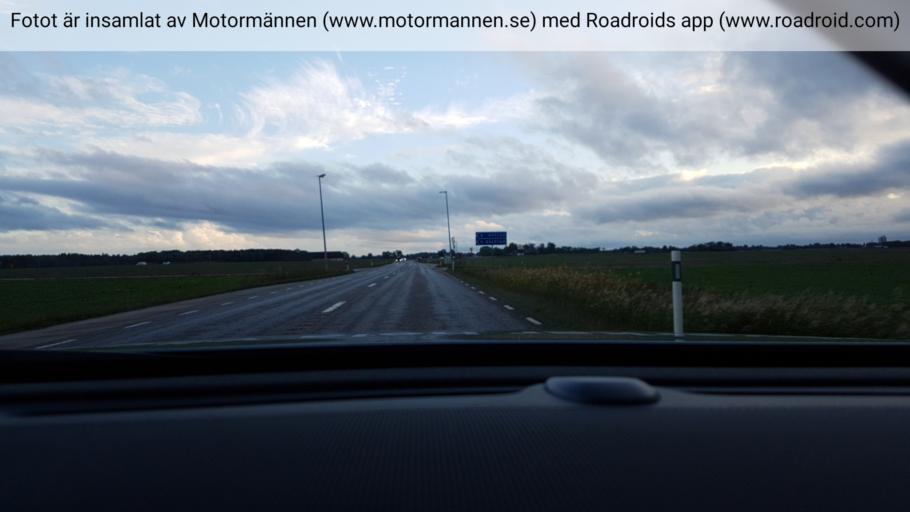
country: SE
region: Vaestra Goetaland
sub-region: Vanersborgs Kommun
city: Bralanda
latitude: 58.5838
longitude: 12.3988
